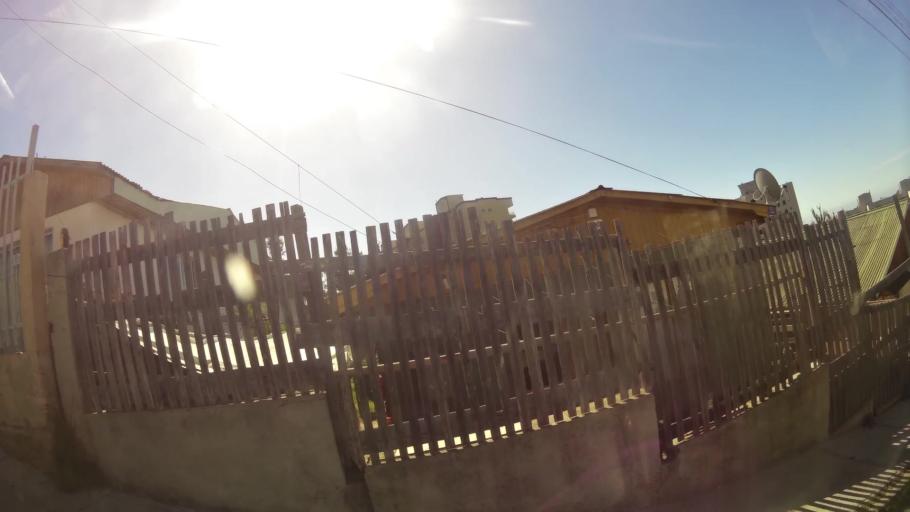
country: CL
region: Valparaiso
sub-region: Provincia de Valparaiso
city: Vina del Mar
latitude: -33.0381
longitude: -71.5628
